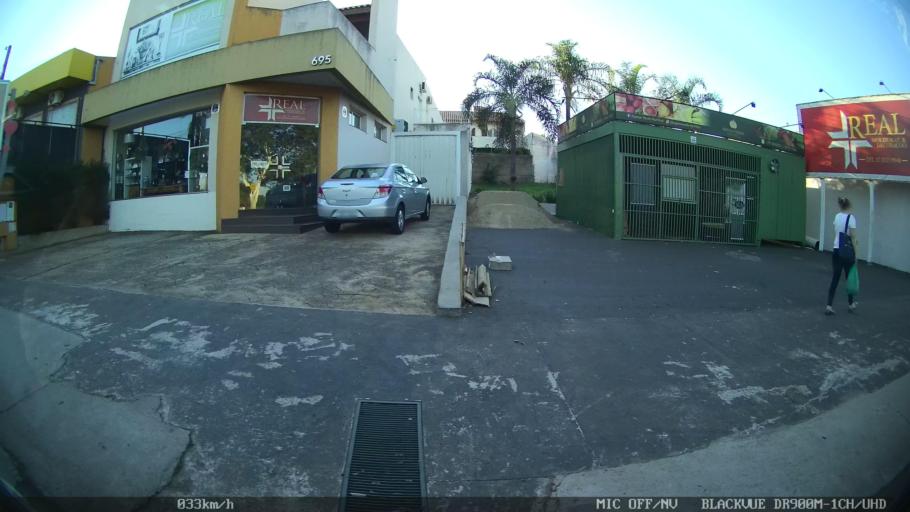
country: BR
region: Sao Paulo
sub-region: Sao Jose Do Rio Preto
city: Sao Jose do Rio Preto
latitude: -20.8079
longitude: -49.3669
